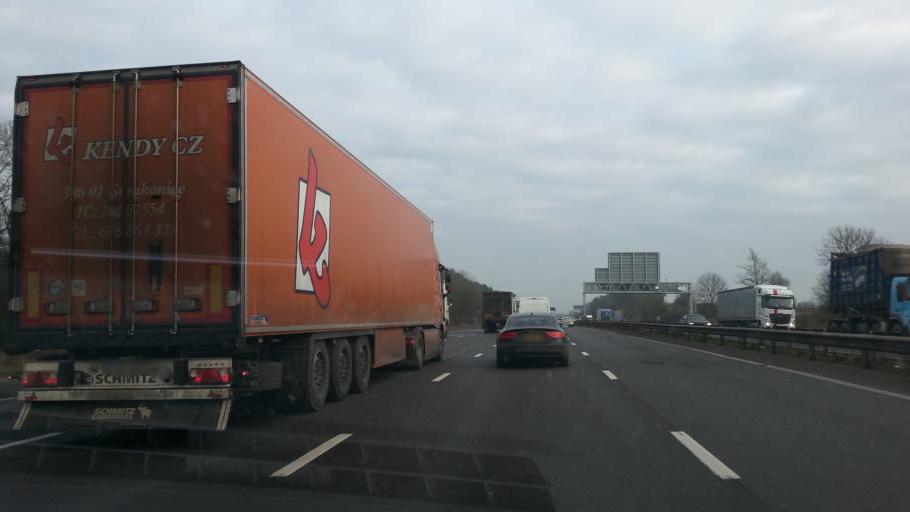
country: GB
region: England
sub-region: Solihull
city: Meriden
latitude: 52.4699
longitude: -1.6476
